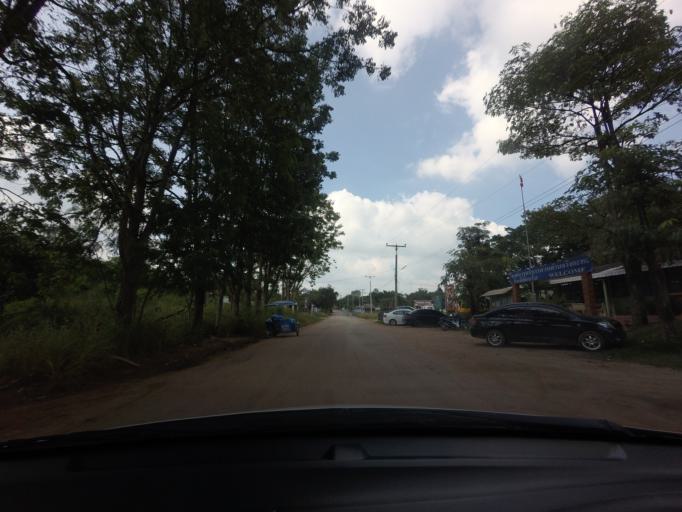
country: TH
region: Nakhon Ratchasima
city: Wang Nam Khiao
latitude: 14.5230
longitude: 101.6264
